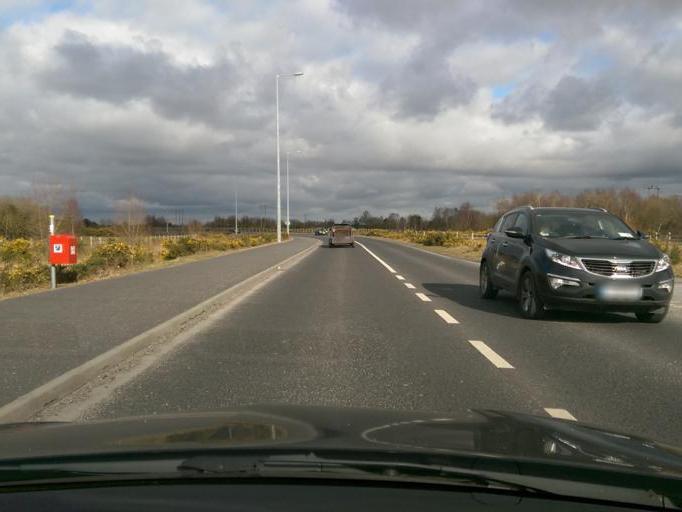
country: IE
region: Leinster
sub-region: An Iarmhi
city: Athlone
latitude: 53.4161
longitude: -7.9783
